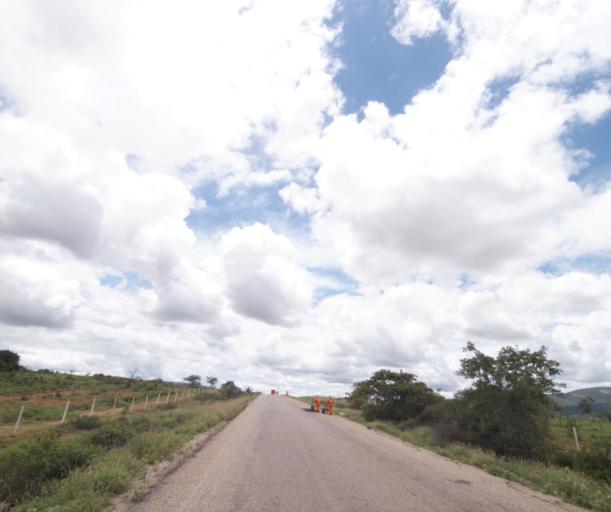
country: BR
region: Bahia
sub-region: Brumado
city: Brumado
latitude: -14.1579
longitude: -41.5227
